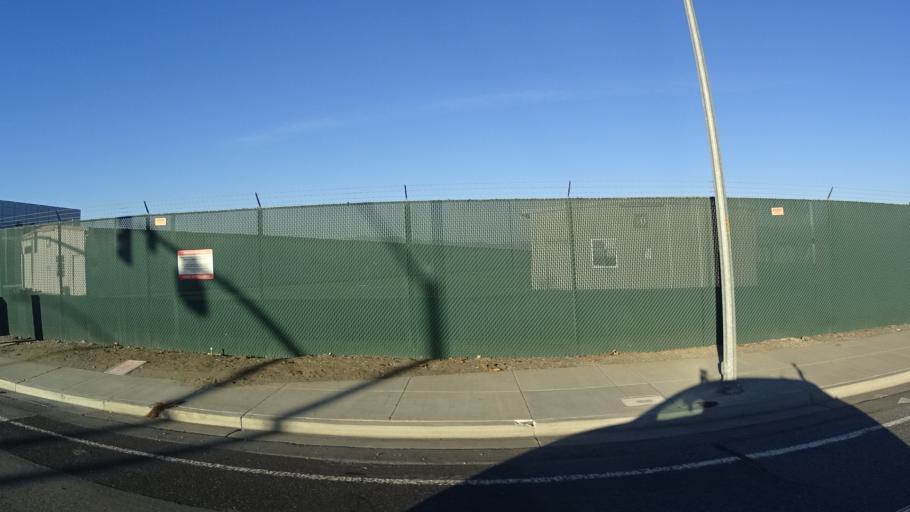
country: US
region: California
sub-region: Santa Clara County
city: Burbank
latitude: 37.3528
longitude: -121.9246
